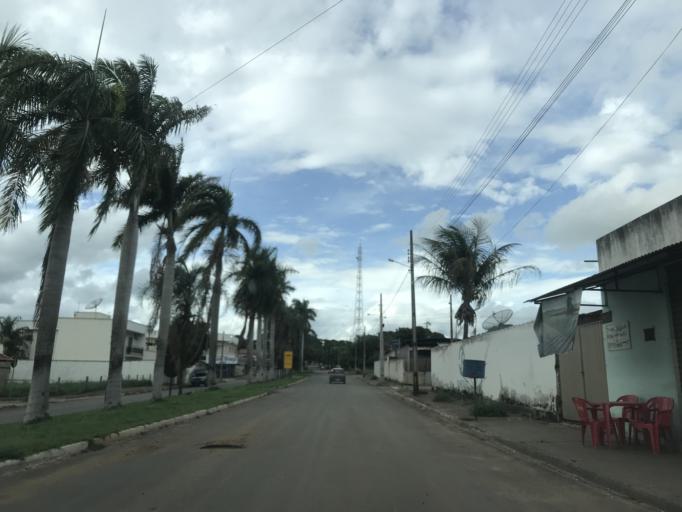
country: BR
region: Goias
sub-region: Bela Vista De Goias
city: Bela Vista de Goias
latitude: -17.0570
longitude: -48.6652
